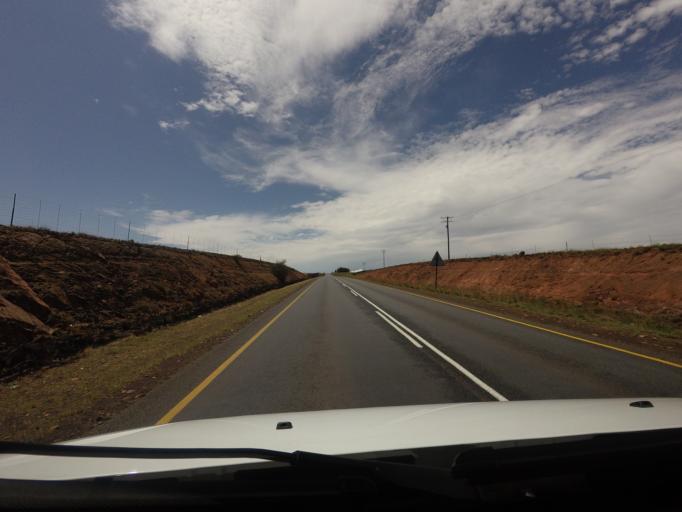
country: ZA
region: Mpumalanga
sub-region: Nkangala District Municipality
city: Belfast
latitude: -25.4021
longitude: 30.1221
